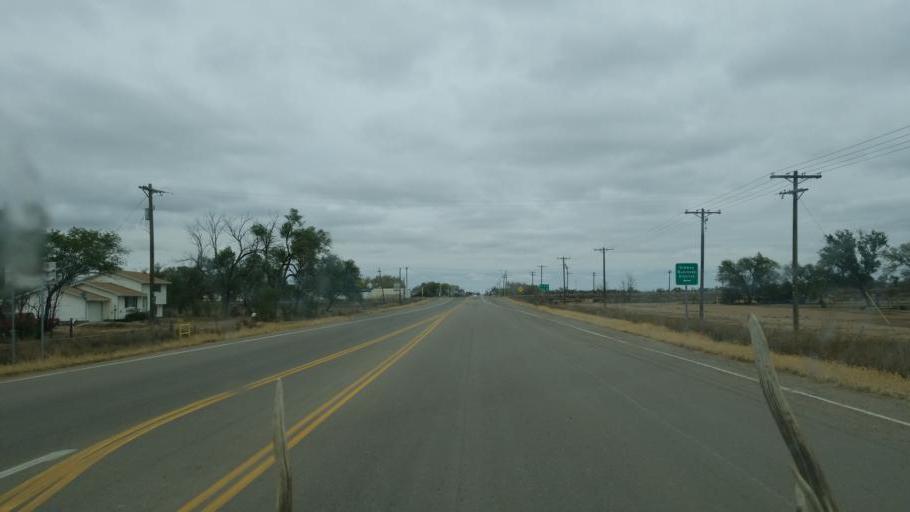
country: US
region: Colorado
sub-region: Crowley County
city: Ordway
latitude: 38.2153
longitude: -103.7481
